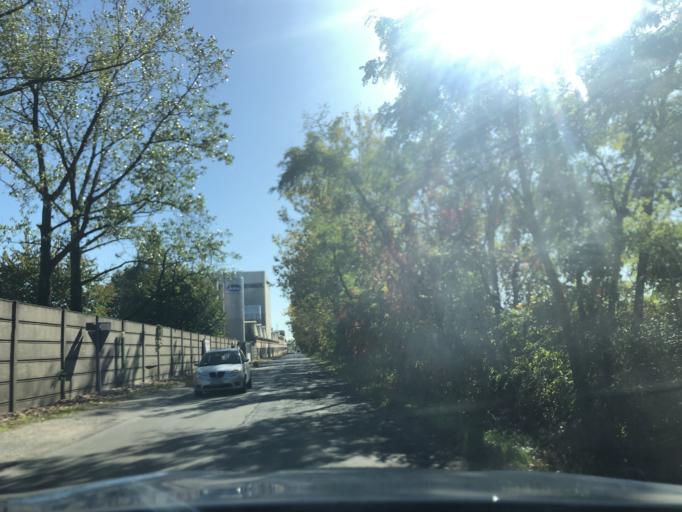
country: IT
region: Lombardy
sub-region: Provincia di Monza e Brianza
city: Barlassina
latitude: 45.6361
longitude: 9.1161
